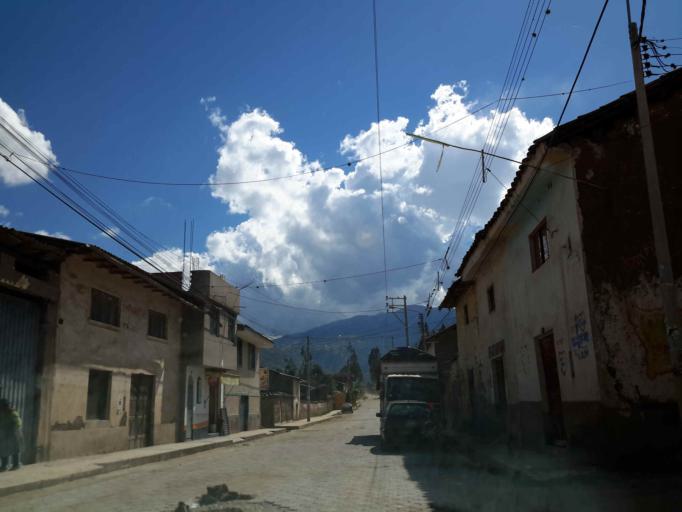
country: PE
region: Apurimac
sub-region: Provincia de Andahuaylas
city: Talavera
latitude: -13.6513
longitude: -73.4346
